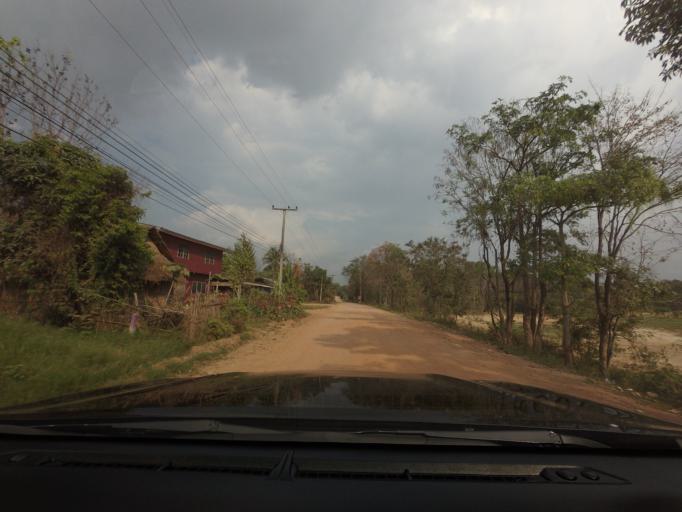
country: TH
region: Nakhon Ratchasima
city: Wang Nam Khiao
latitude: 14.4427
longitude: 101.6765
